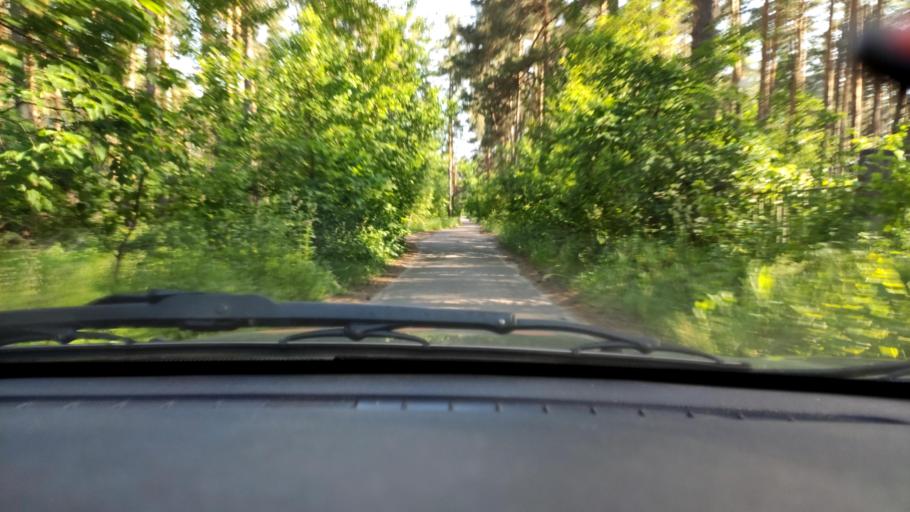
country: RU
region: Voronezj
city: Somovo
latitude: 51.7562
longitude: 39.3745
